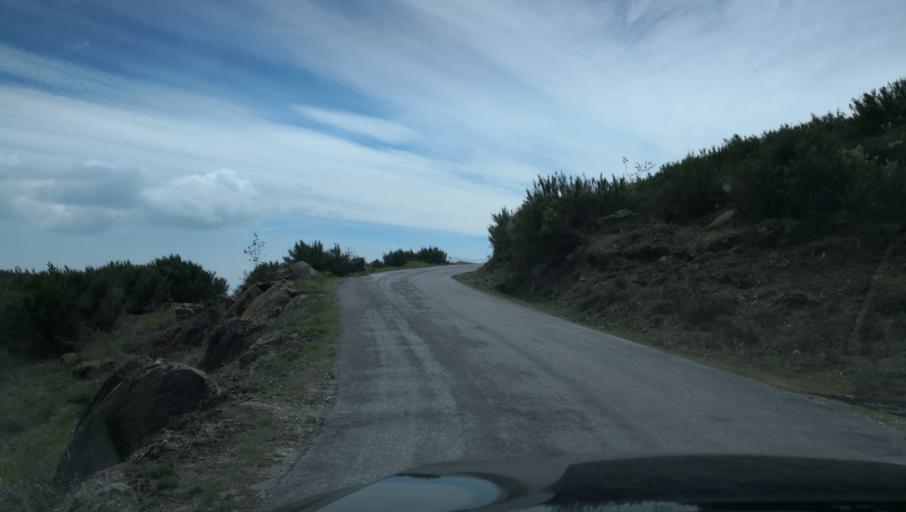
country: PT
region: Vila Real
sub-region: Vila Real
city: Vila Real
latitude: 41.3021
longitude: -7.8110
